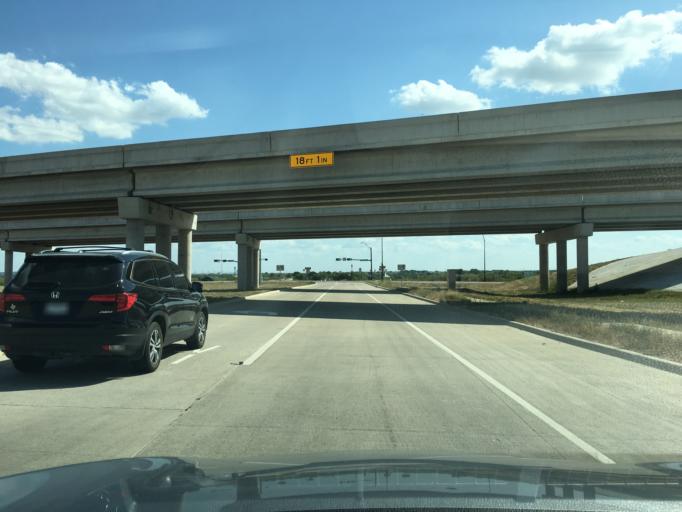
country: US
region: Texas
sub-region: Tarrant County
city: Mansfield
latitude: 32.5235
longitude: -97.0832
